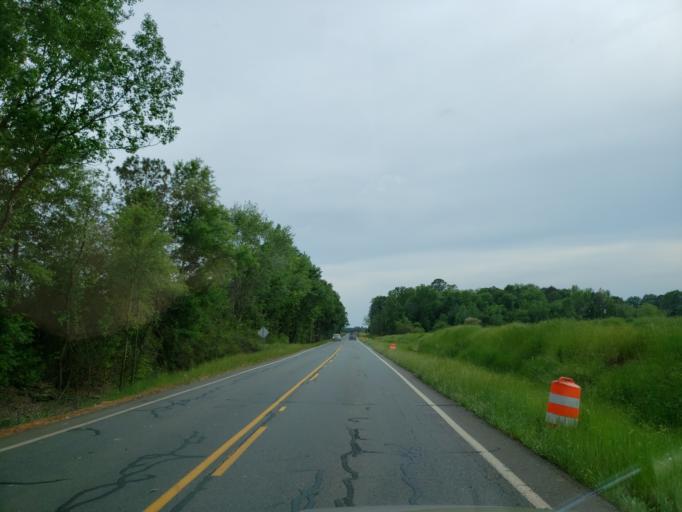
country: US
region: Georgia
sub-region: Macon County
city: Marshallville
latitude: 32.3767
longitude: -83.8887
